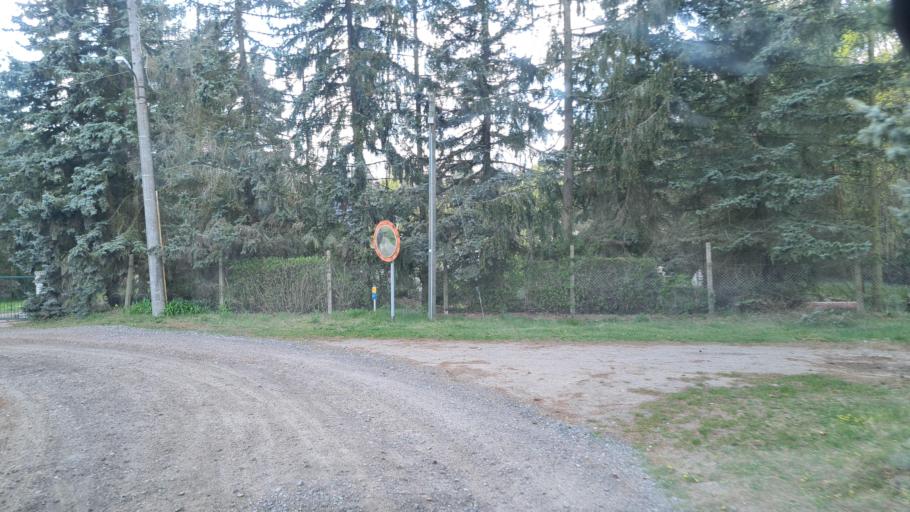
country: DE
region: Brandenburg
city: Luckenwalde
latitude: 52.0874
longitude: 13.1338
